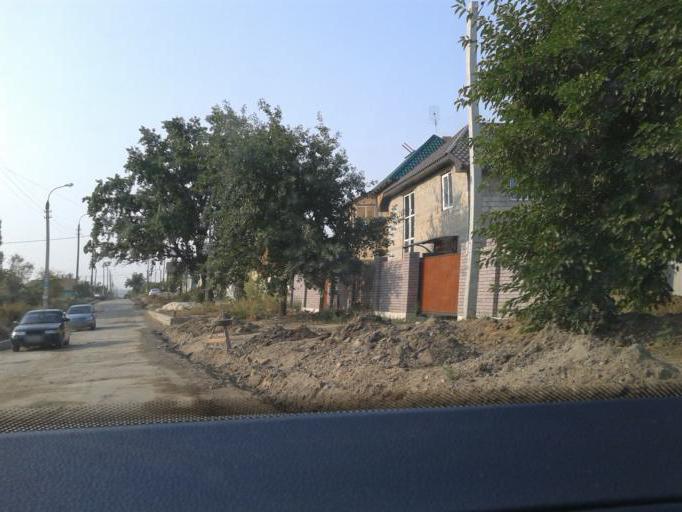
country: RU
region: Volgograd
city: Volgograd
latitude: 48.6144
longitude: 44.4139
